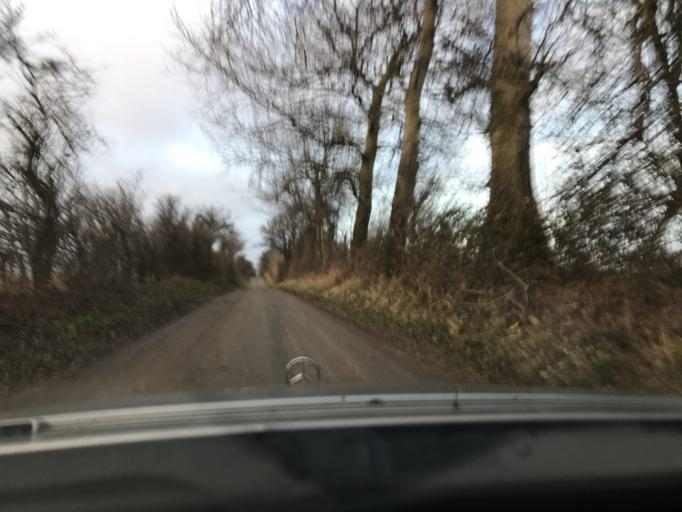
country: DK
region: South Denmark
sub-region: Sonderborg Kommune
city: Nordborg
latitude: 55.0585
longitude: 9.6714
